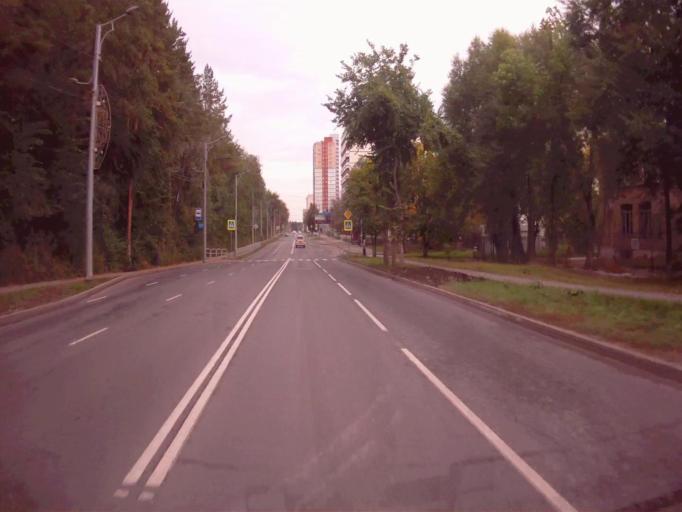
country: RU
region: Chelyabinsk
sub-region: Gorod Chelyabinsk
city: Chelyabinsk
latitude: 55.1519
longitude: 61.3651
